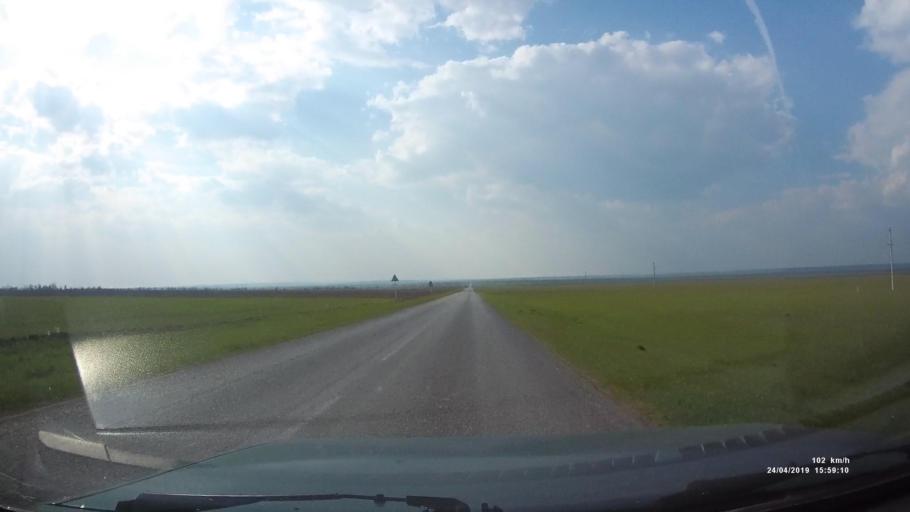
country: RU
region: Rostov
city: Sovetskoye
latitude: 46.6209
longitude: 42.4769
